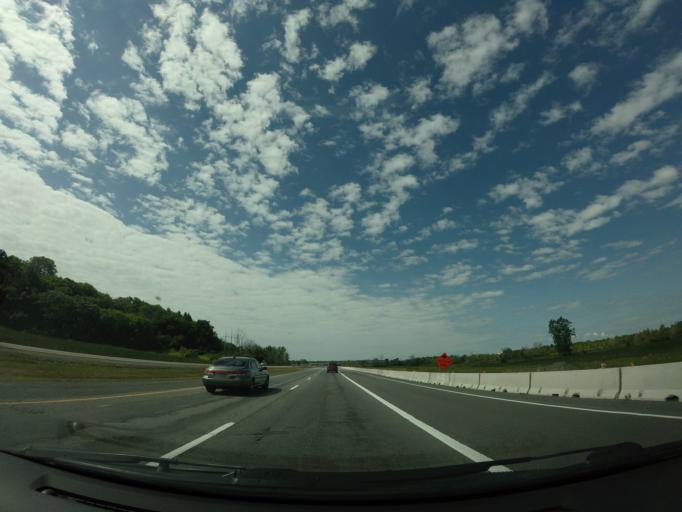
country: CA
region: Quebec
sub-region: Outaouais
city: Gatineau
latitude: 45.4614
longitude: -75.5660
